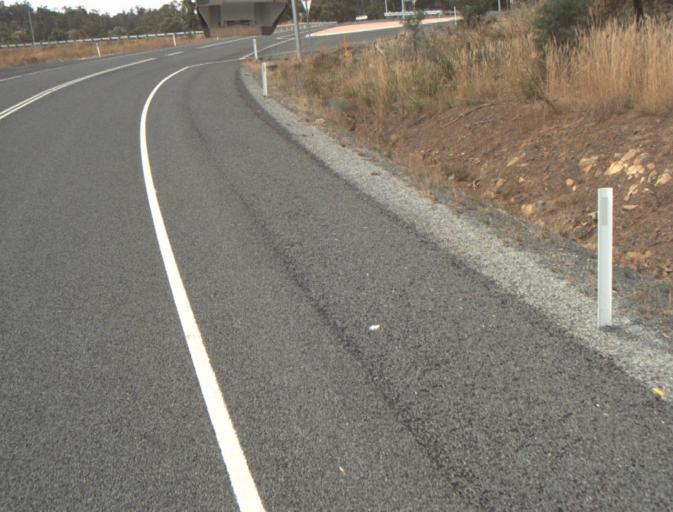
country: AU
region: Tasmania
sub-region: Launceston
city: Mayfield
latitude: -41.3029
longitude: 147.0491
